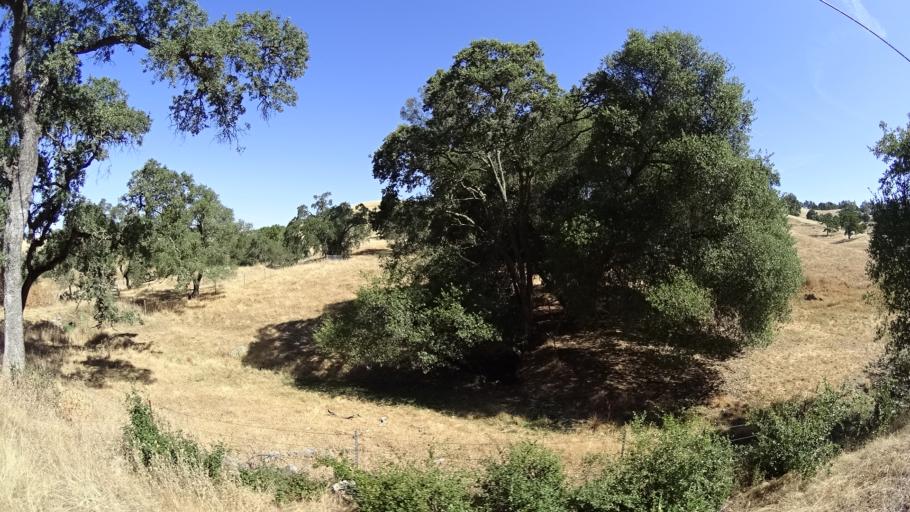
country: US
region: California
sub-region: Calaveras County
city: Valley Springs
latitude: 38.2294
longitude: -120.8482
